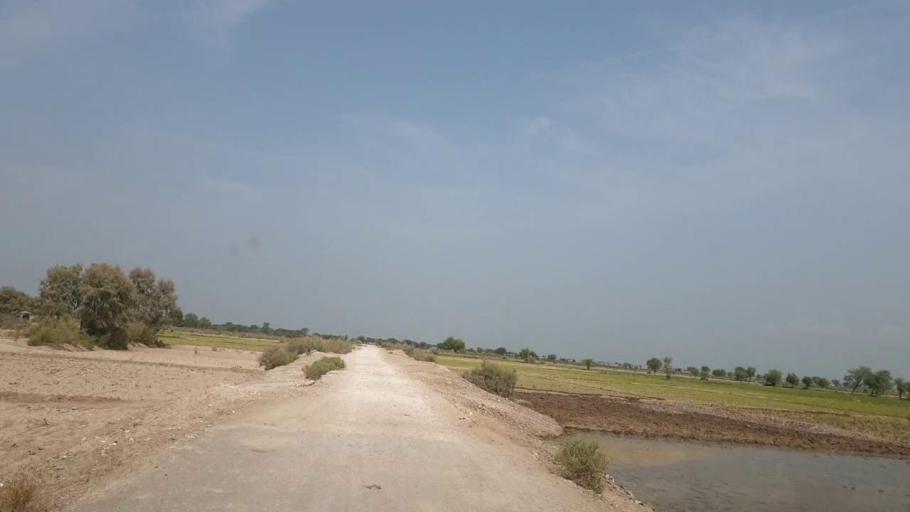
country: PK
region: Sindh
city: Dokri
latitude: 27.3990
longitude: 68.2549
